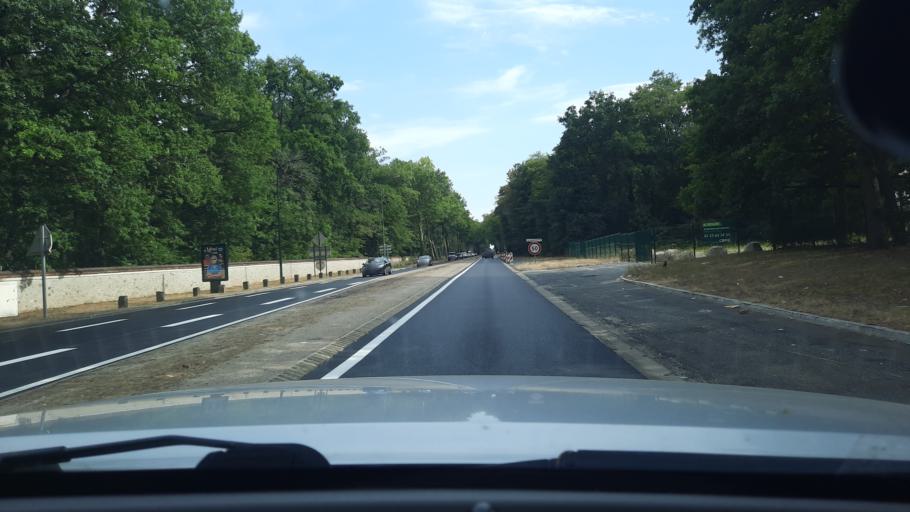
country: FR
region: Ile-de-France
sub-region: Departement de Seine-et-Marne
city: Dammarie-les-Lys
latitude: 48.5174
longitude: 2.6551
